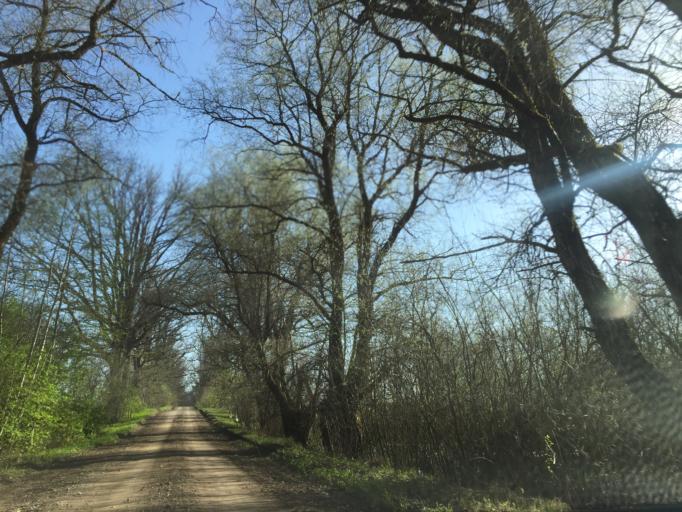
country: LV
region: Ergli
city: Ergli
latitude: 56.8756
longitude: 25.4834
